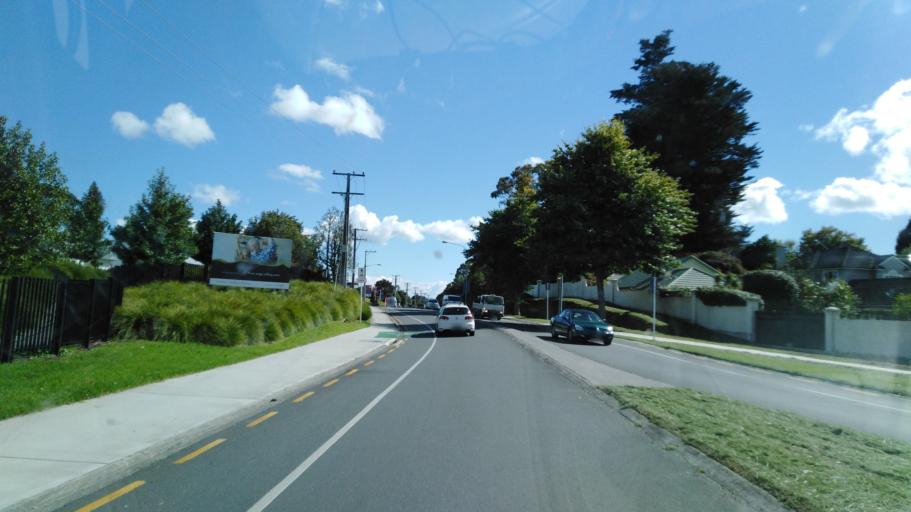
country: NZ
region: Bay of Plenty
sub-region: Tauranga City
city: Tauranga
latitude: -37.7006
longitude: 176.1132
